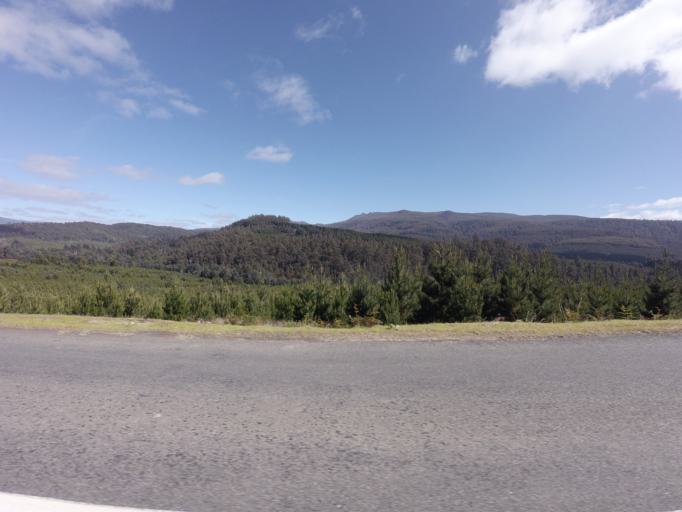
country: AU
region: Tasmania
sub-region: Derwent Valley
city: New Norfolk
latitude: -42.7444
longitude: 146.6549
